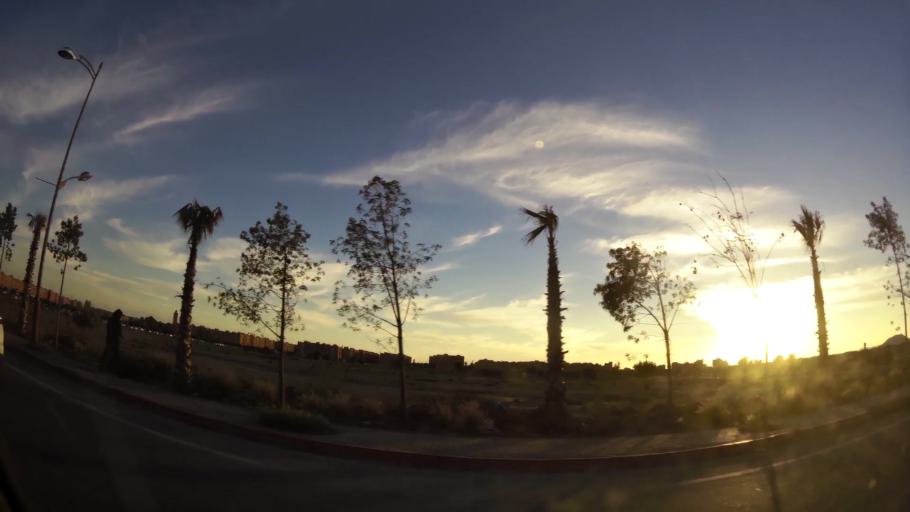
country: MA
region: Marrakech-Tensift-Al Haouz
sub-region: Marrakech
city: Marrakesh
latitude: 31.7559
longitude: -8.1121
